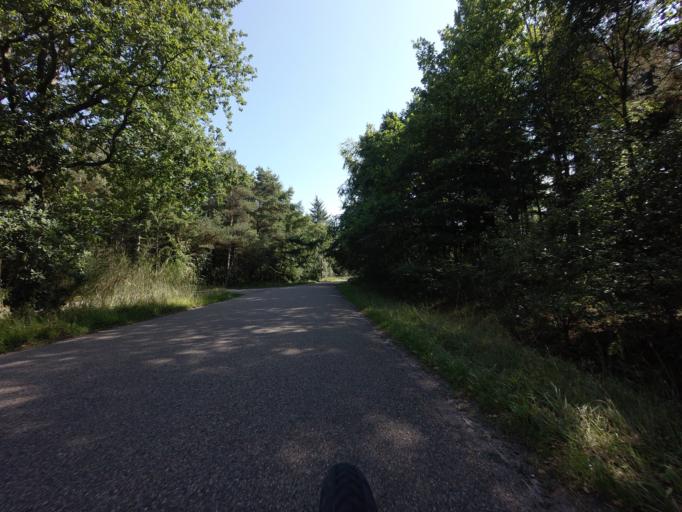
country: DK
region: North Denmark
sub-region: Hjorring Kommune
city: Hirtshals
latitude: 57.5824
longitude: 10.0017
